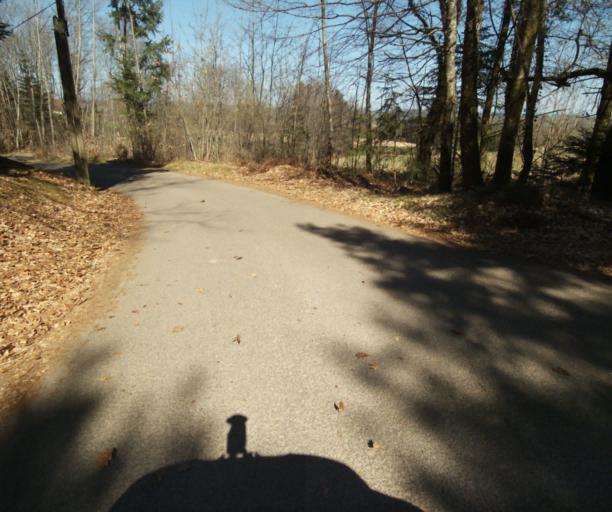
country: FR
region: Limousin
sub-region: Departement de la Correze
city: Saint-Mexant
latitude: 45.2925
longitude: 1.7000
